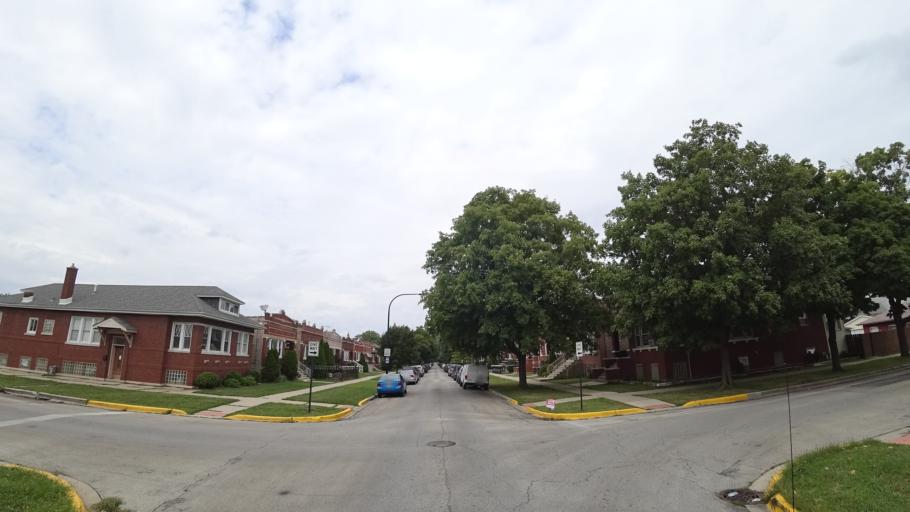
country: US
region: Illinois
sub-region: Cook County
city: Cicero
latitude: 41.8526
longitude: -87.7713
